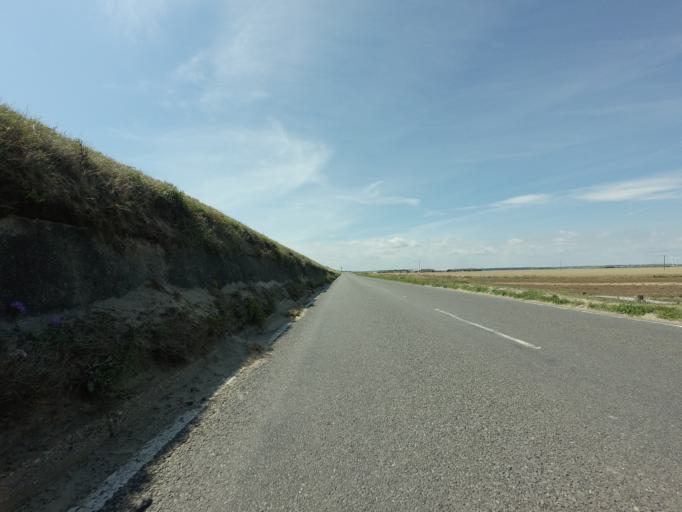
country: GB
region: England
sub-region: Kent
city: Lydd
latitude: 50.9288
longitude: 0.8231
